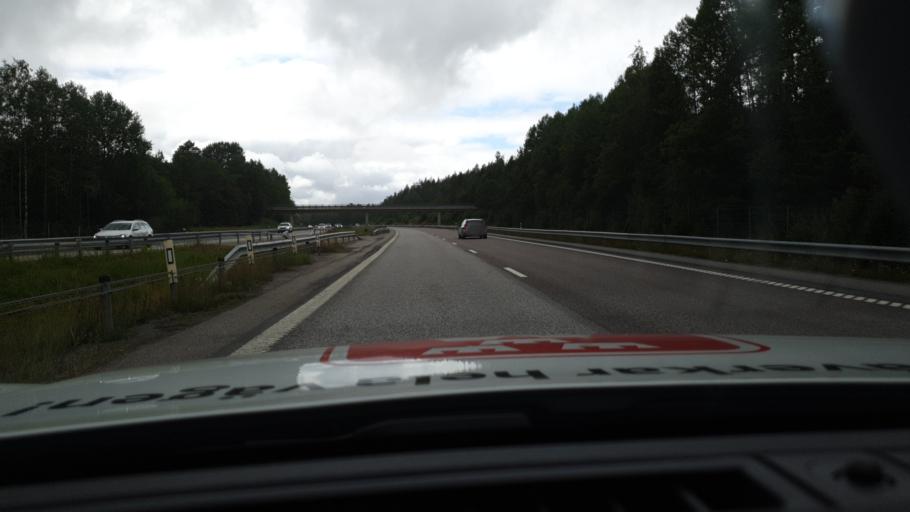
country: SE
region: Stockholm
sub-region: Norrtalje Kommun
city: Norrtalje
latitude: 59.7430
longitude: 18.6070
